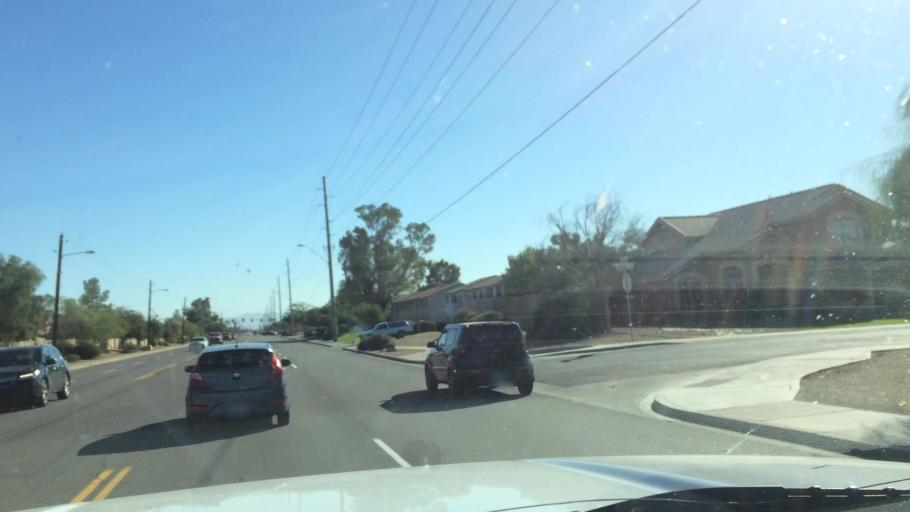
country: US
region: Arizona
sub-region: Maricopa County
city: Peoria
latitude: 33.5917
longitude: -112.2203
